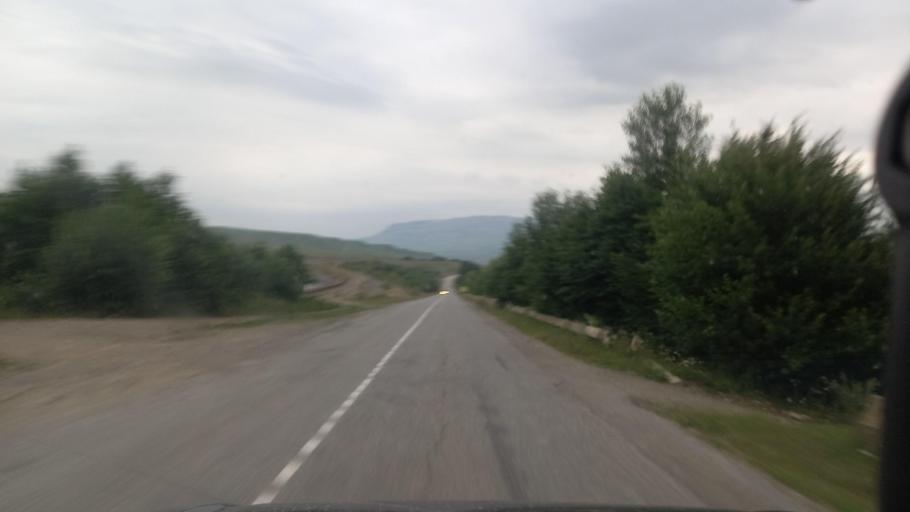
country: RU
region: Karachayevo-Cherkesiya
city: Mednogorskiy
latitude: 43.9411
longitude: 41.1509
